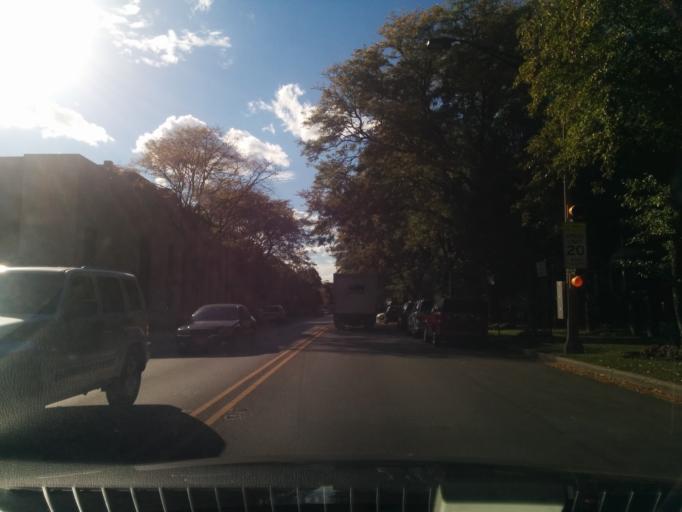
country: US
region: Illinois
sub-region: Cook County
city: Forest Park
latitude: 41.8883
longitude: -87.8168
